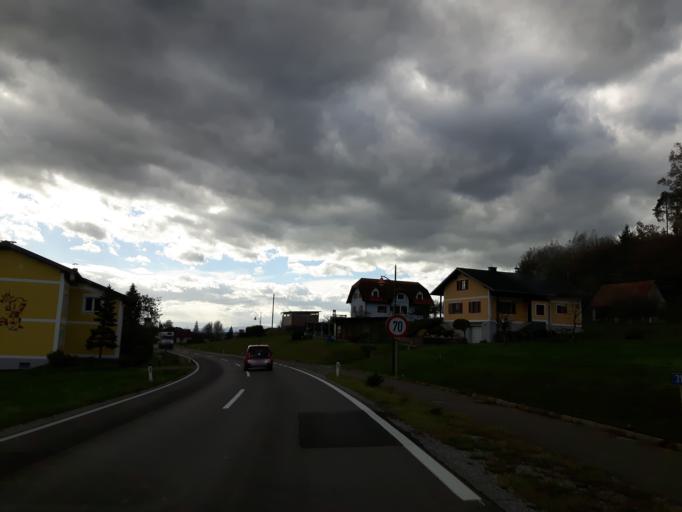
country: AT
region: Styria
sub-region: Politischer Bezirk Suedoststeiermark
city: Kirchbach in Steiermark
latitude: 46.9036
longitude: 15.6673
